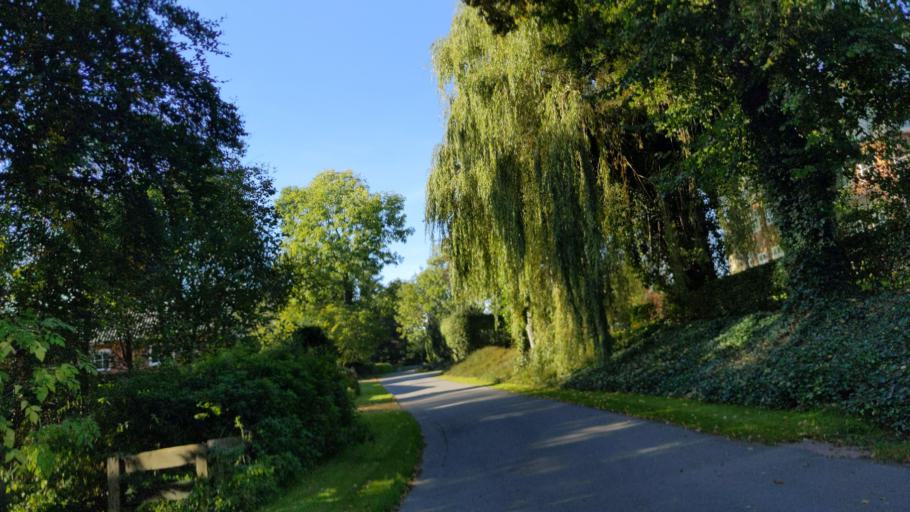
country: DE
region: Schleswig-Holstein
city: Ahrensbok
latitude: 54.0639
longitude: 10.5805
